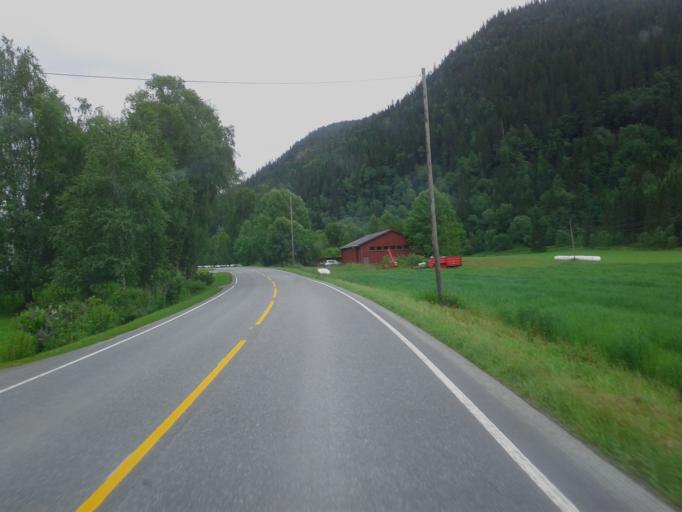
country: NO
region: Sor-Trondelag
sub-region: Midtre Gauldal
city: Storen
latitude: 63.0133
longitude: 10.3642
